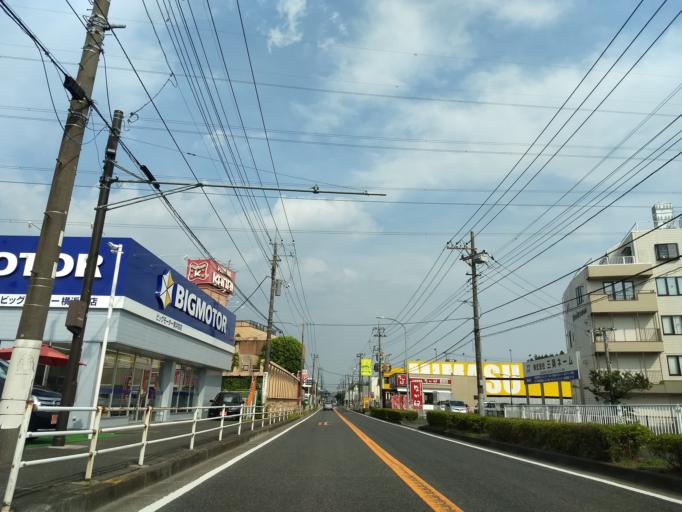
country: JP
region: Kanagawa
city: Minami-rinkan
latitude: 35.4951
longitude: 139.5051
